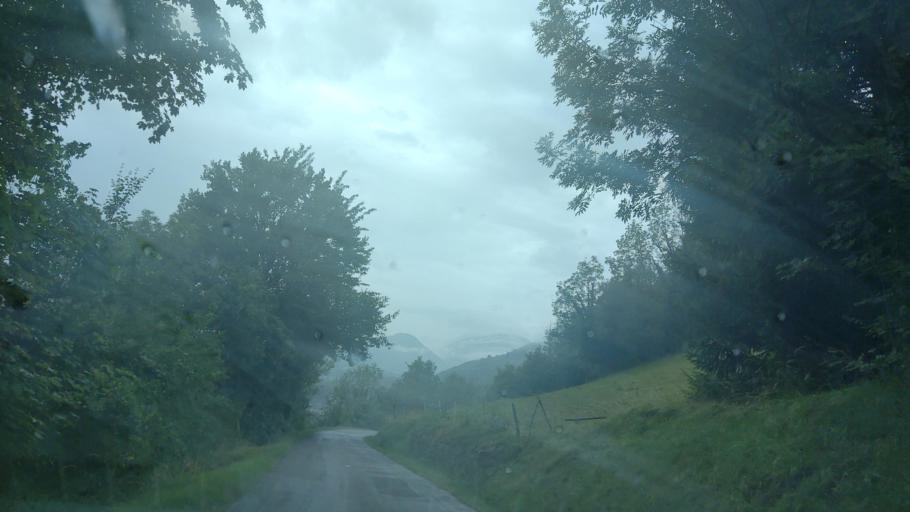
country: FR
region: Rhone-Alpes
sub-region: Departement de la Savoie
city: Coise-Saint-Jean-Pied-Gauthier
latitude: 45.5039
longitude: 6.1505
